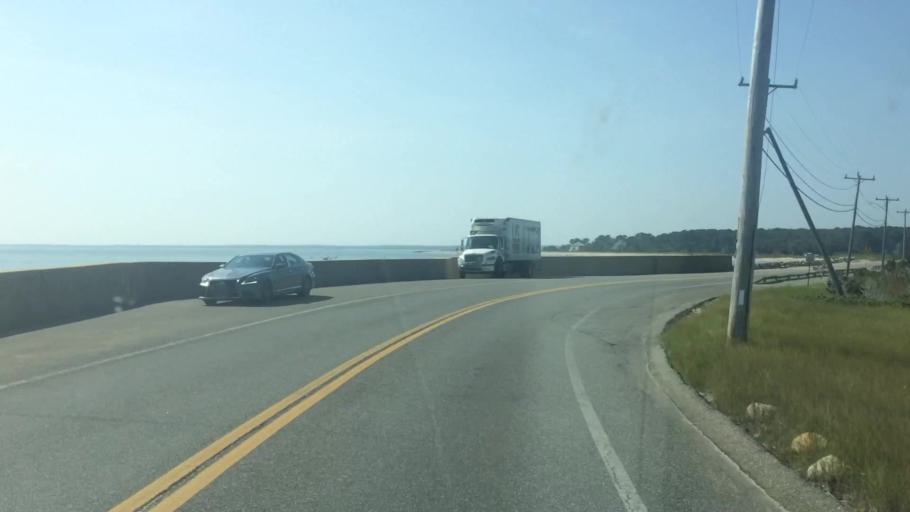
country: US
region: Massachusetts
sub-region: Dukes County
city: Oak Bluffs
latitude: 41.4491
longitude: -70.5529
